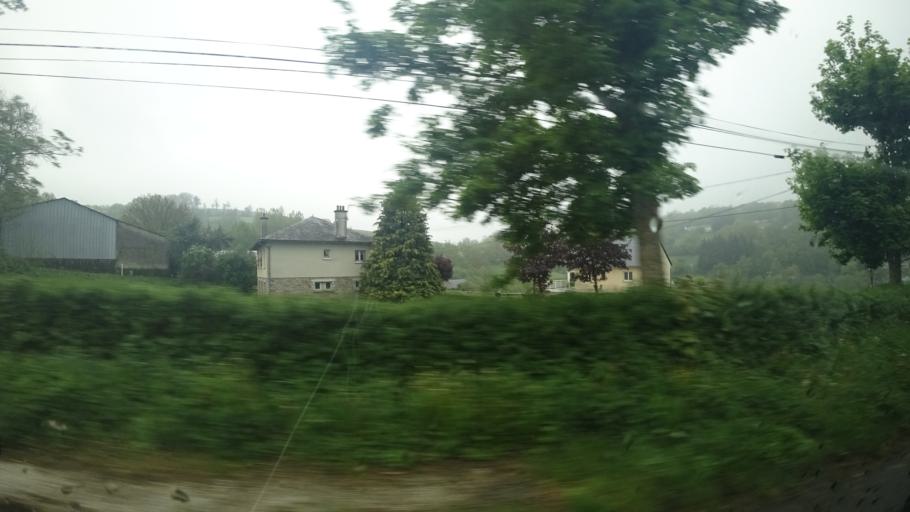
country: FR
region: Midi-Pyrenees
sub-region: Departement de l'Aveyron
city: Laissac
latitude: 44.2902
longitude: 2.8377
